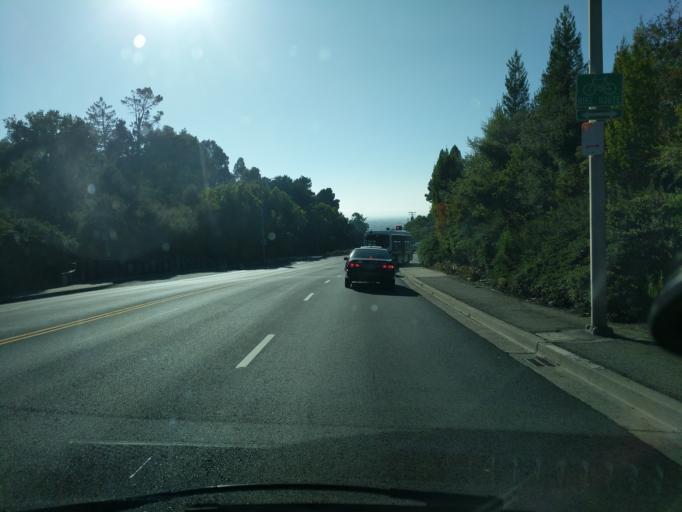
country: US
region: California
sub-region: Alameda County
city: Hayward
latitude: 37.6588
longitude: -122.0622
